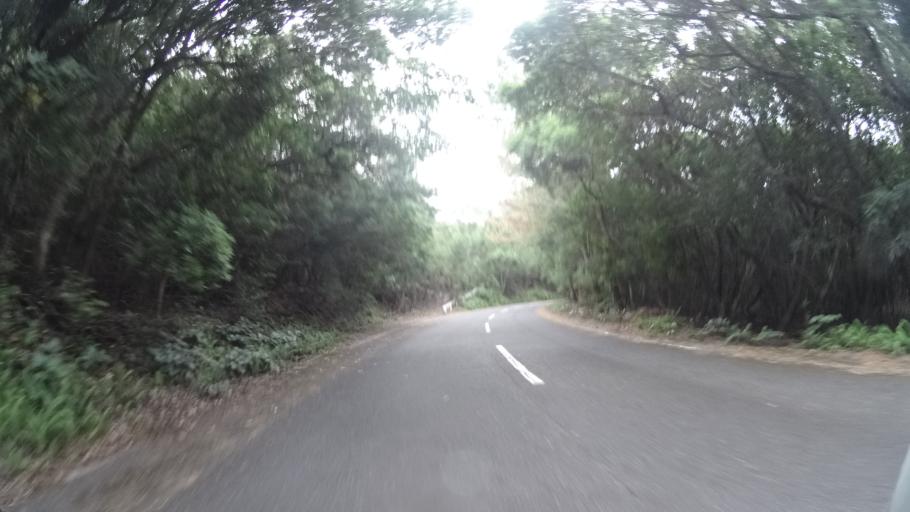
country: JP
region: Kagoshima
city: Nishinoomote
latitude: 30.2992
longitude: 130.4118
